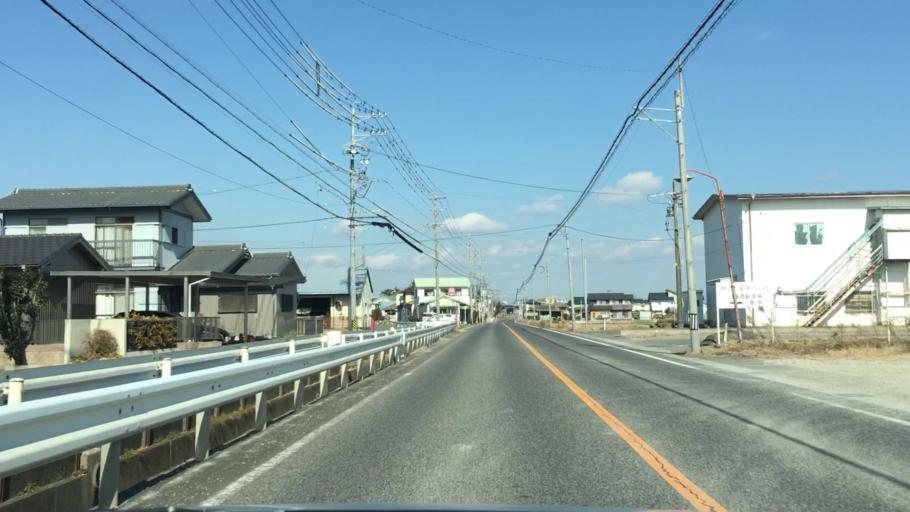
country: JP
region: Aichi
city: Anjo
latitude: 35.0029
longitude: 137.1175
